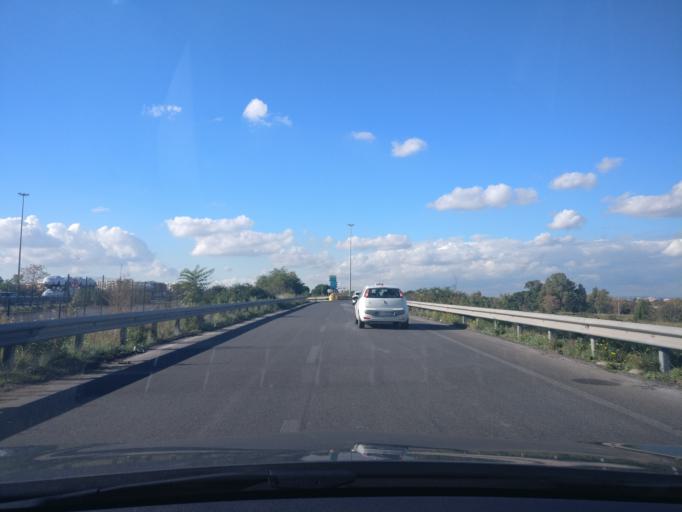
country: IT
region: Latium
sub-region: Citta metropolitana di Roma Capitale
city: Ciampino
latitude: 41.8520
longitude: 12.6015
